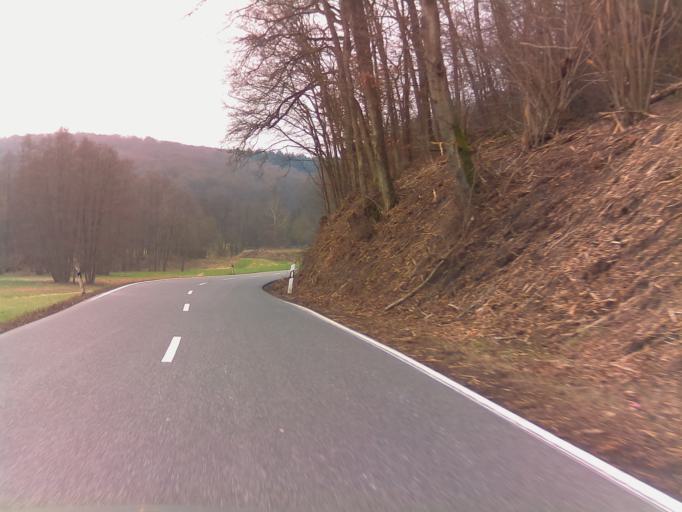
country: DE
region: Rheinland-Pfalz
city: Staudernheim
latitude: 49.7626
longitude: 7.6725
